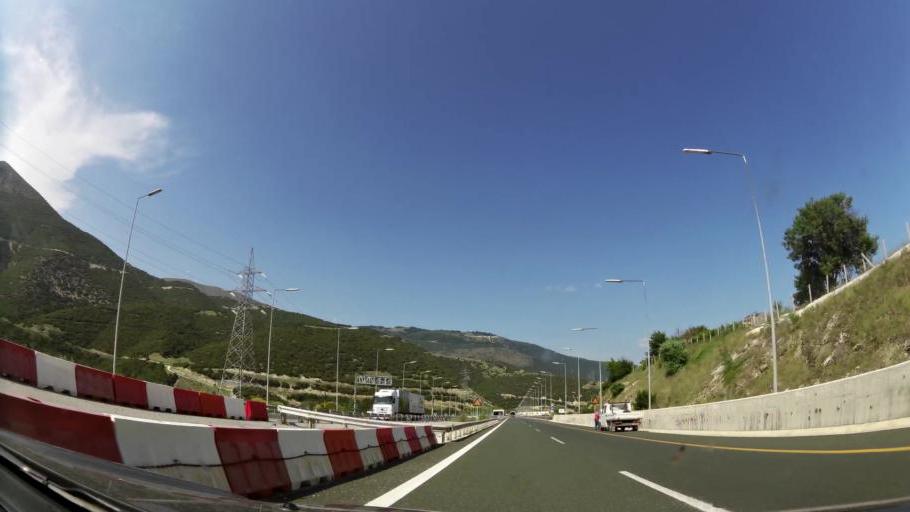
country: GR
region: West Macedonia
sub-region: Nomos Kozanis
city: Velventos
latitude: 40.3689
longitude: 22.0778
